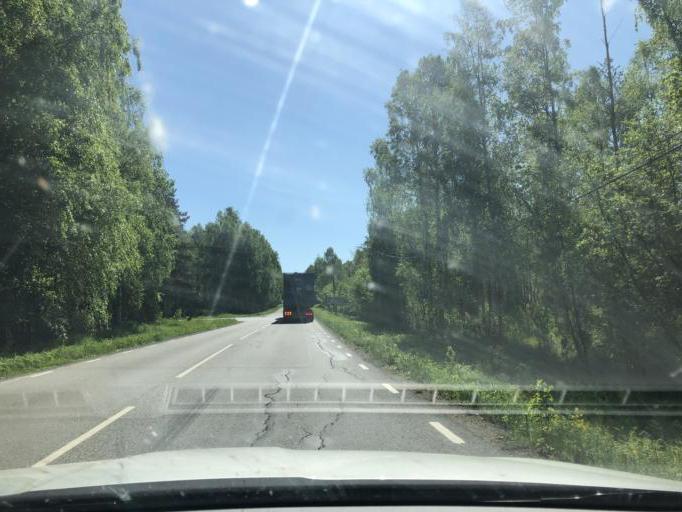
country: SE
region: Norrbotten
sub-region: Lulea Kommun
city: Sodra Sunderbyn
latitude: 65.6640
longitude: 21.9688
